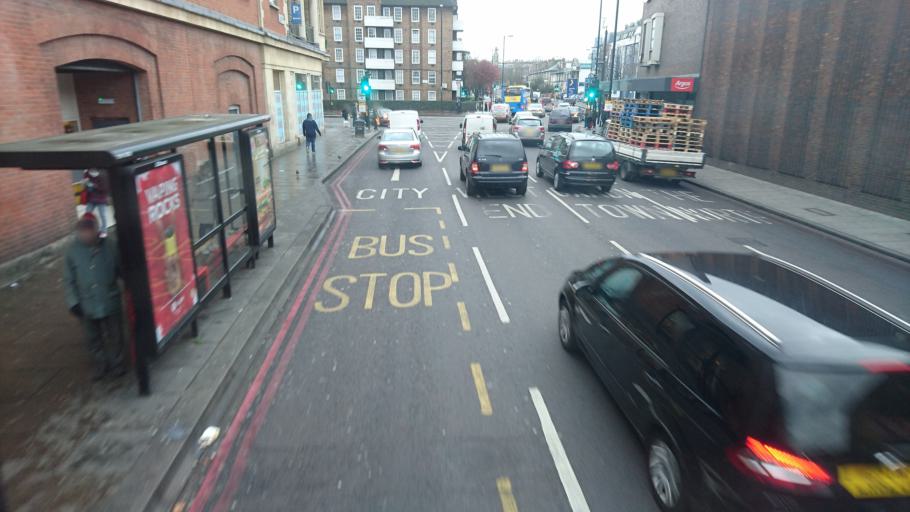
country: GB
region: England
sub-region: Greater London
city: Holloway
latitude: 51.5564
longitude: -0.1162
